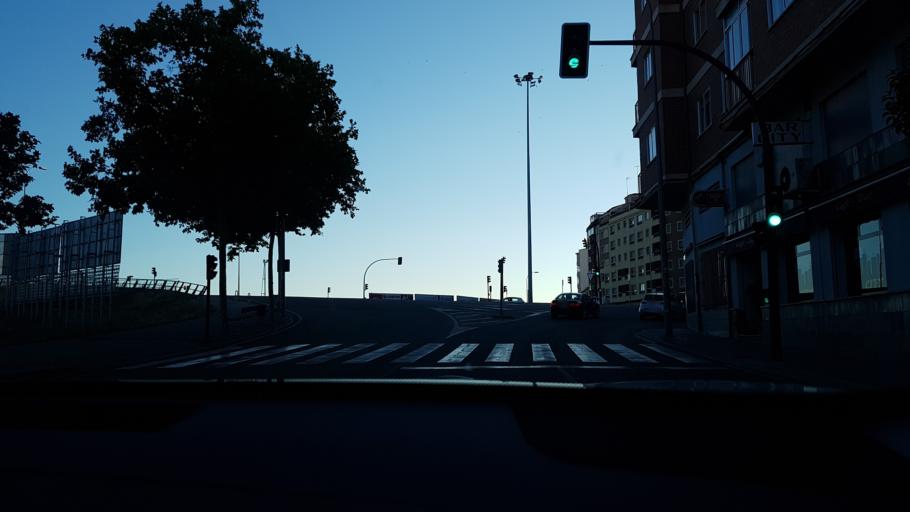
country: ES
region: Castille and Leon
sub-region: Provincia de Zamora
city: Zamora
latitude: 41.5134
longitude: -5.7441
